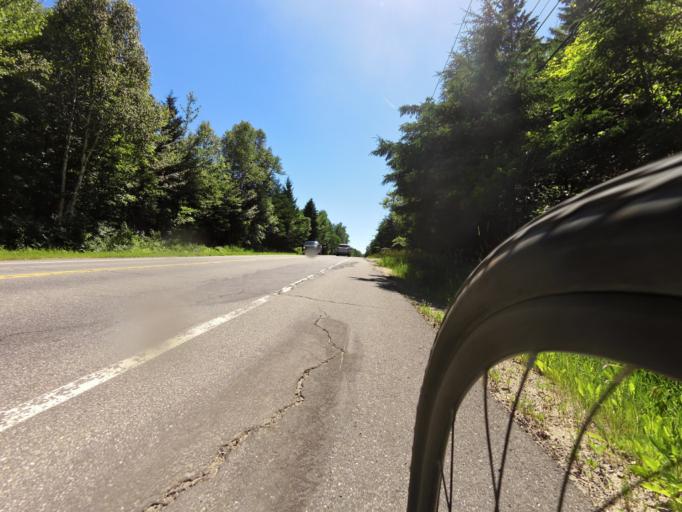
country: CA
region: Quebec
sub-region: Laurentides
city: Mont-Tremblant
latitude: 46.0984
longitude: -74.6193
